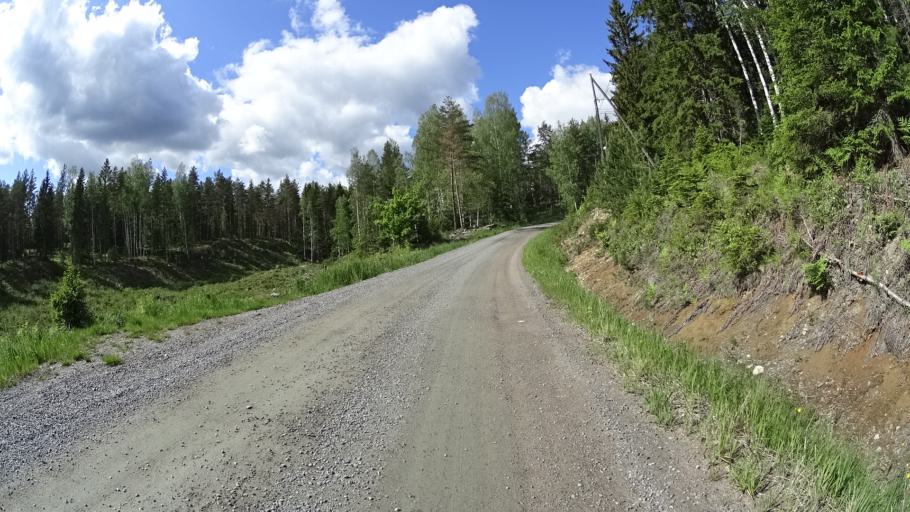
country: FI
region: Uusimaa
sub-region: Raaseporin
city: Pohja
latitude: 60.1743
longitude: 23.5854
